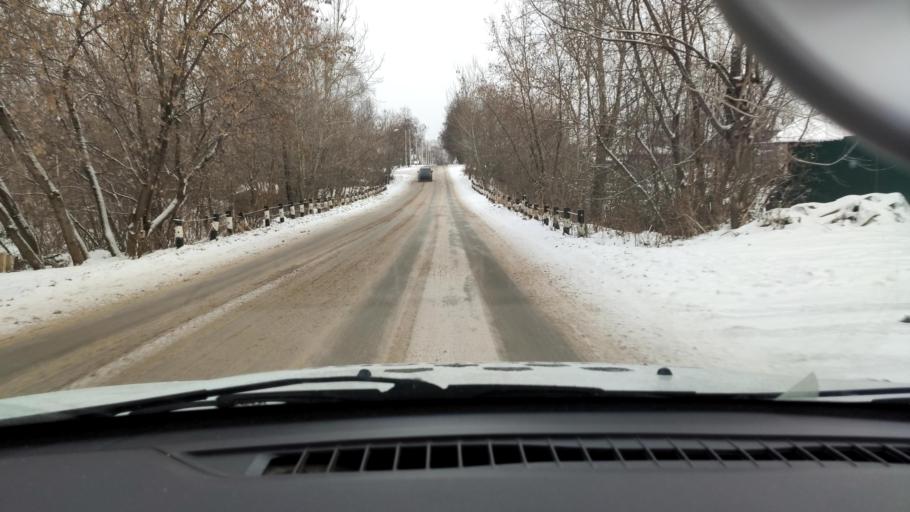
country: RU
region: Perm
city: Polazna
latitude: 58.1203
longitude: 56.3951
